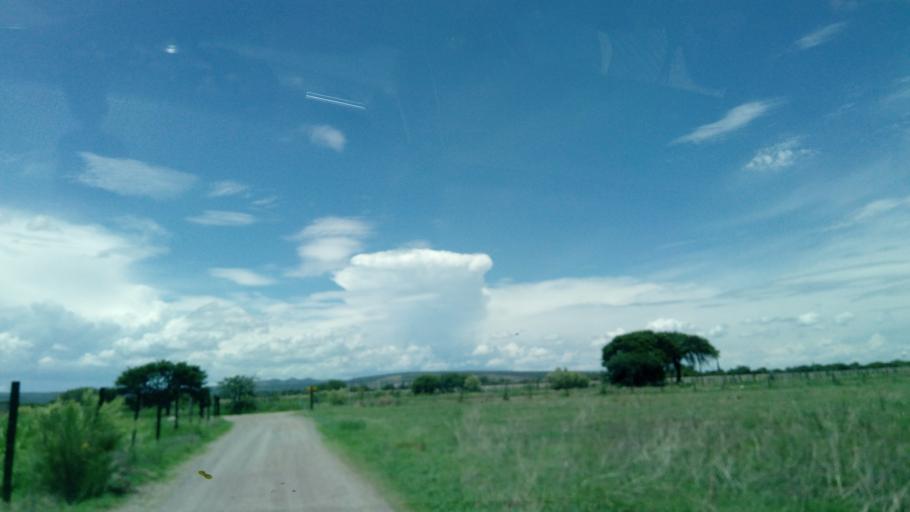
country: MX
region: Durango
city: Victoria de Durango
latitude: 24.0864
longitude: -104.5557
